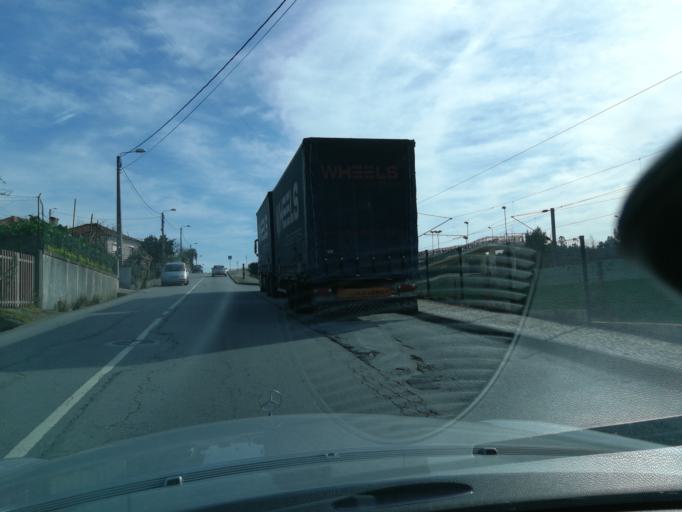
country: PT
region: Braga
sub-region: Vila Nova de Famalicao
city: Vila Nova de Famalicao
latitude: 41.4305
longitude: -8.5225
